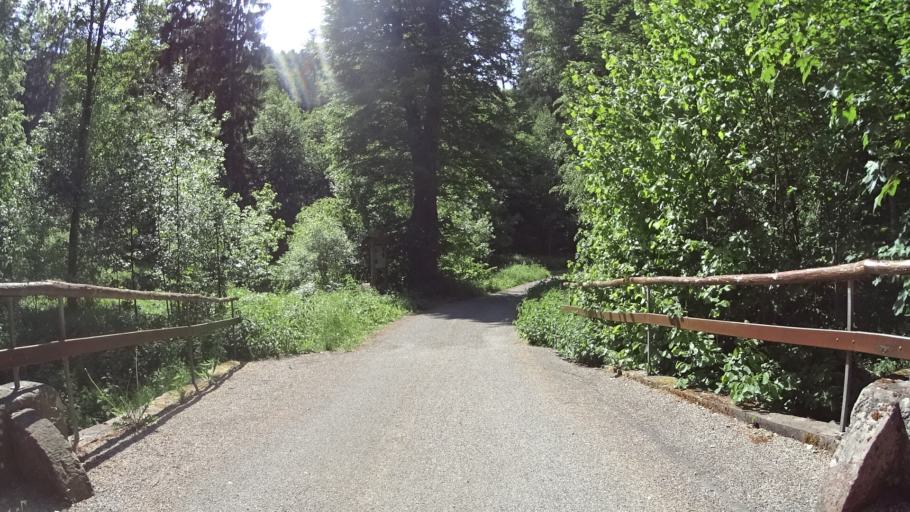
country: DE
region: Baden-Wuerttemberg
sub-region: Karlsruhe Region
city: Hopfingen
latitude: 49.6395
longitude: 9.4382
